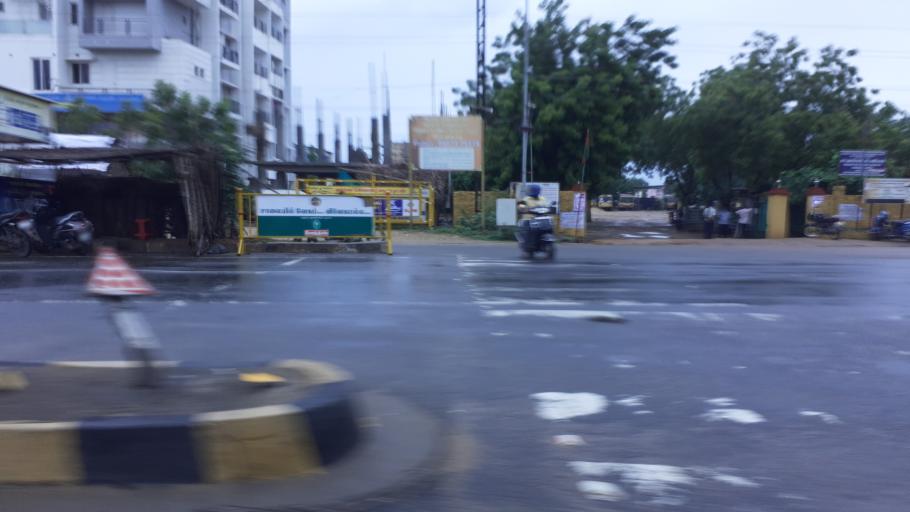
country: IN
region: Tamil Nadu
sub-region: Tirunelveli Kattabo
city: Tirunelveli
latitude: 8.7138
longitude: 77.7732
